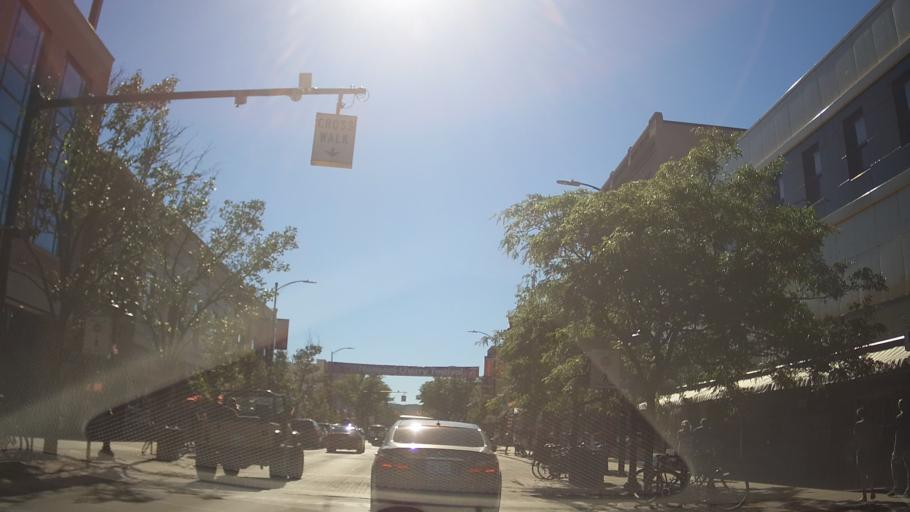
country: US
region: Michigan
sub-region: Grand Traverse County
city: Traverse City
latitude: 44.7641
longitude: -85.6187
